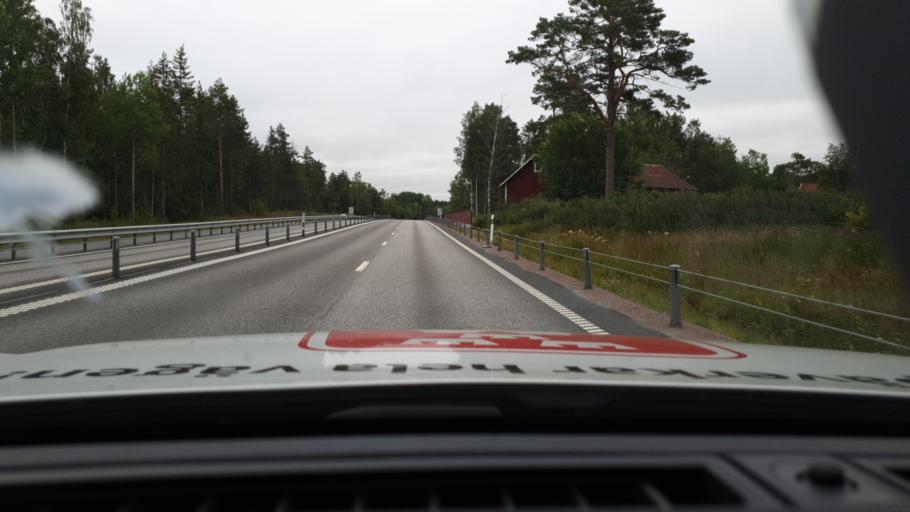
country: SE
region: Uppsala
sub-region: Osthammars Kommun
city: Gimo
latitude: 60.1109
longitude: 18.1293
